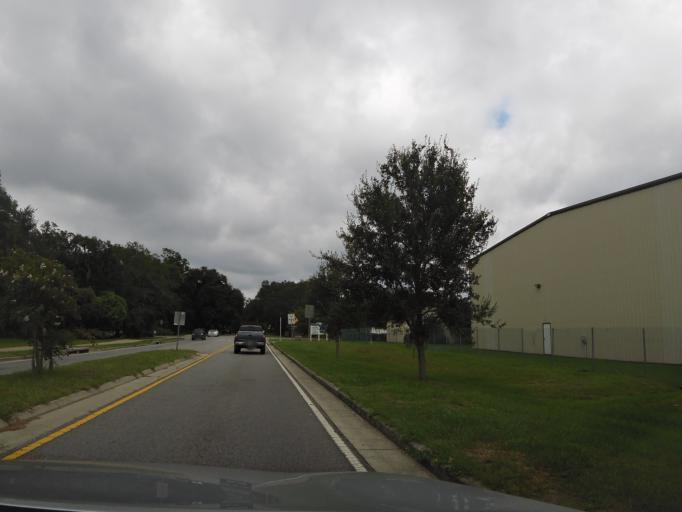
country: US
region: Georgia
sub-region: Glynn County
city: Saint Simons Island
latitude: 31.1520
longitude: -81.3835
